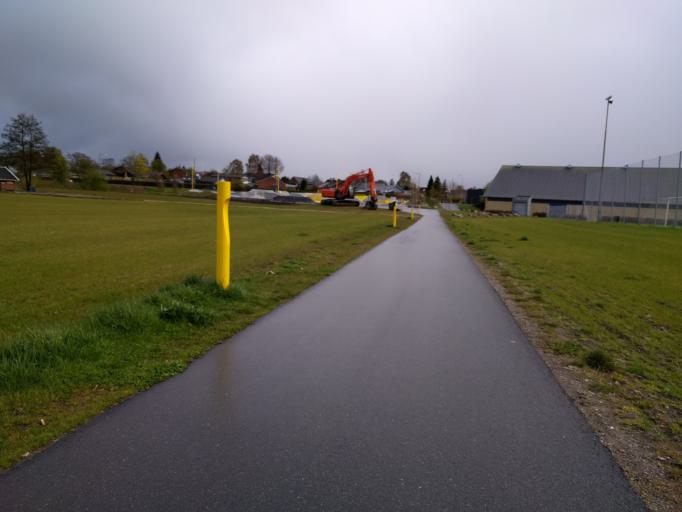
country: DK
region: South Denmark
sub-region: Kerteminde Kommune
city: Munkebo
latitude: 55.4565
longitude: 10.5475
